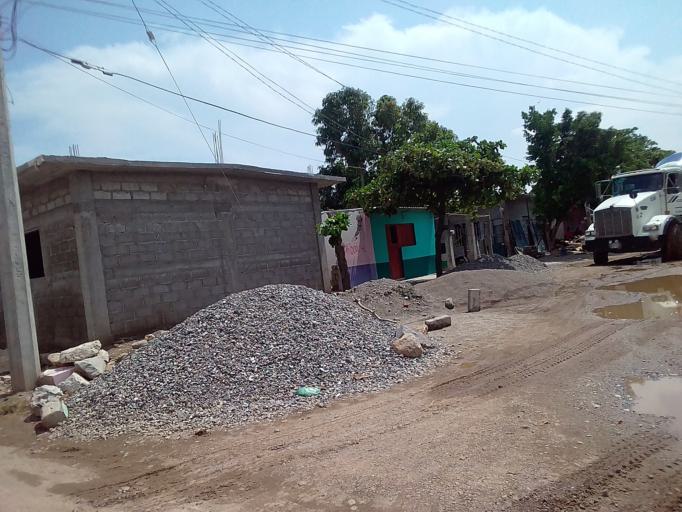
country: MX
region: Oaxaca
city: Union Hidalgo
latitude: 16.4672
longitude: -94.8287
